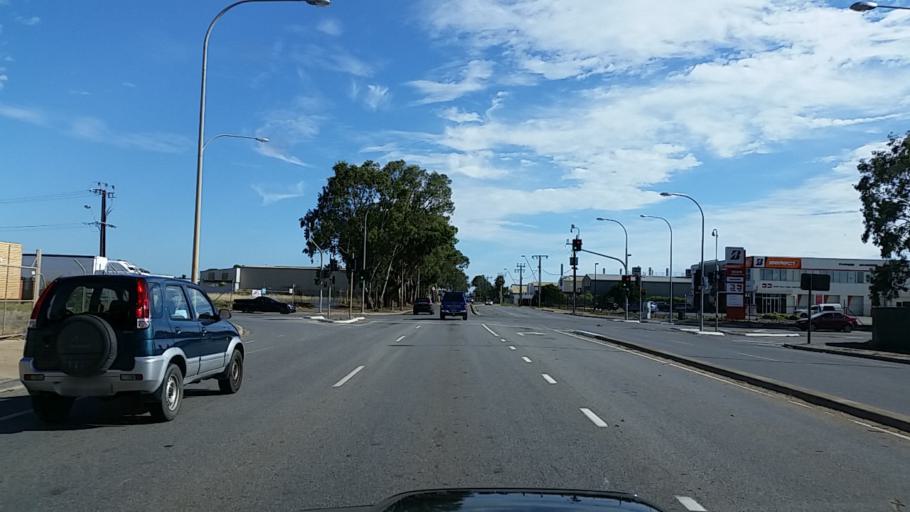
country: AU
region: South Australia
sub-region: Port Adelaide Enfield
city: Alberton
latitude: -34.8408
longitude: 138.5461
